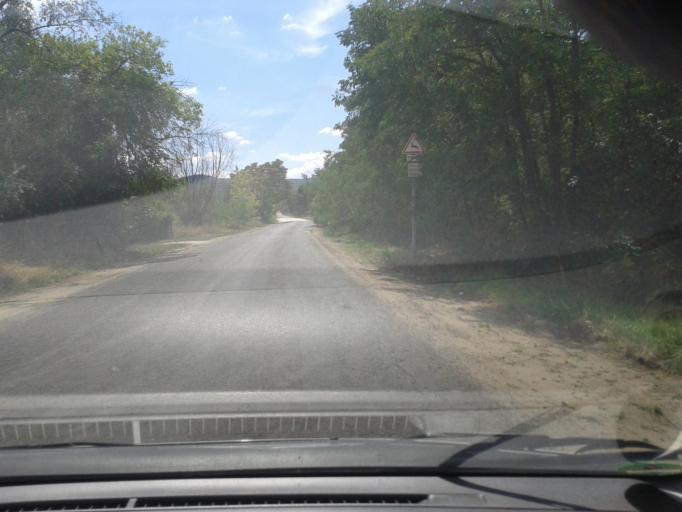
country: HU
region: Komarom-Esztergom
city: Pilismarot
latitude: 47.7959
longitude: 18.8856
